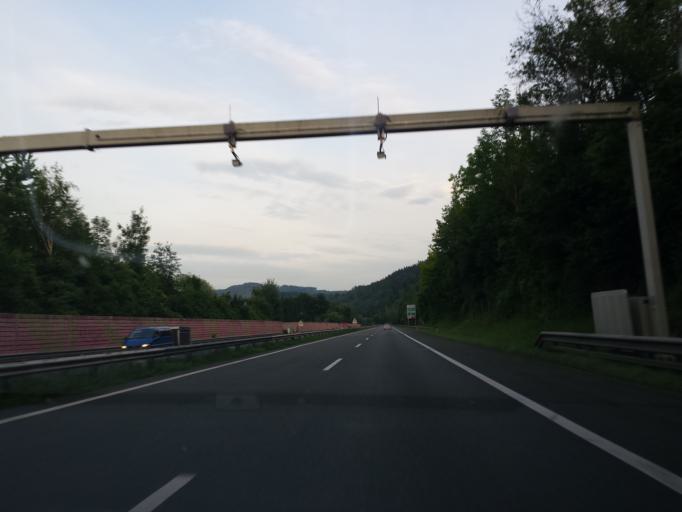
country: AT
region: Styria
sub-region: Politischer Bezirk Graz-Umgebung
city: Deutschfeistritz
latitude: 47.2134
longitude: 15.3067
